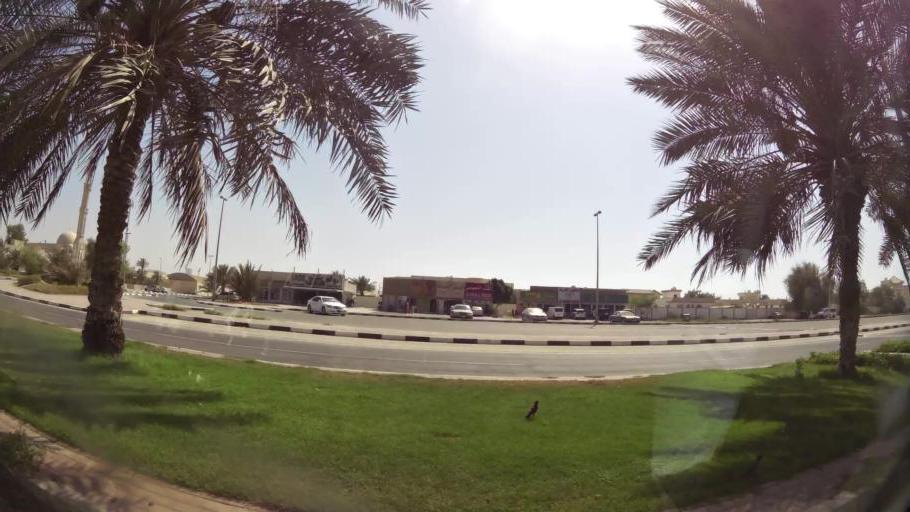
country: AE
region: Ajman
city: Ajman
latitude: 25.4170
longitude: 55.4706
